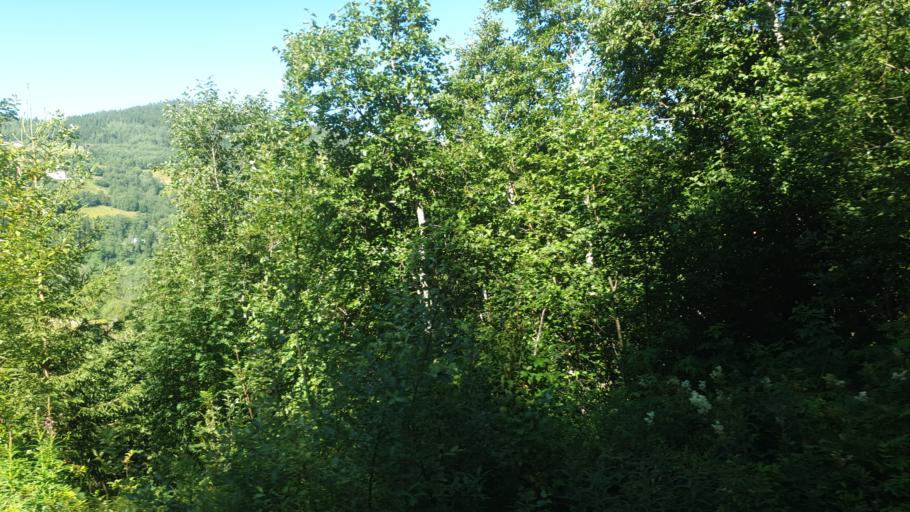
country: NO
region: Sor-Trondelag
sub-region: Meldal
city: Meldal
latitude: 63.1662
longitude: 9.7401
